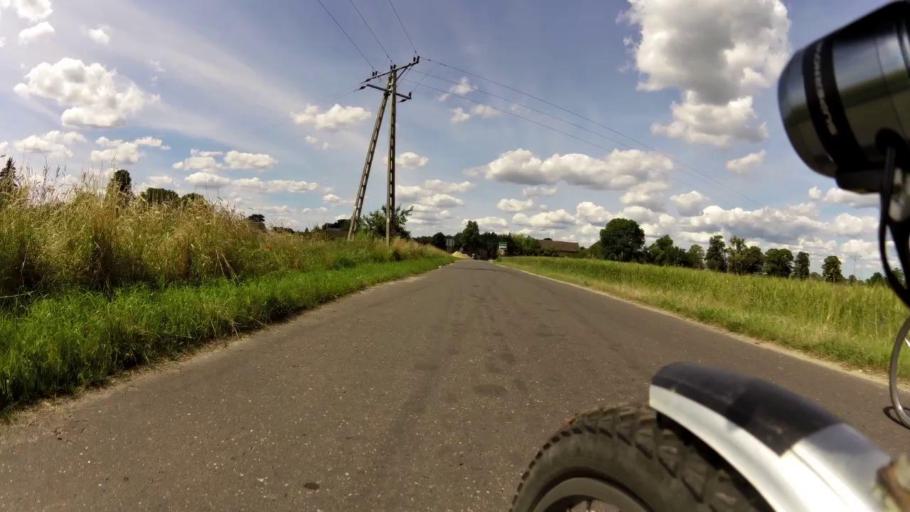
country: PL
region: West Pomeranian Voivodeship
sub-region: Powiat lobeski
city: Wegorzyno
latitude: 53.5359
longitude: 15.4364
